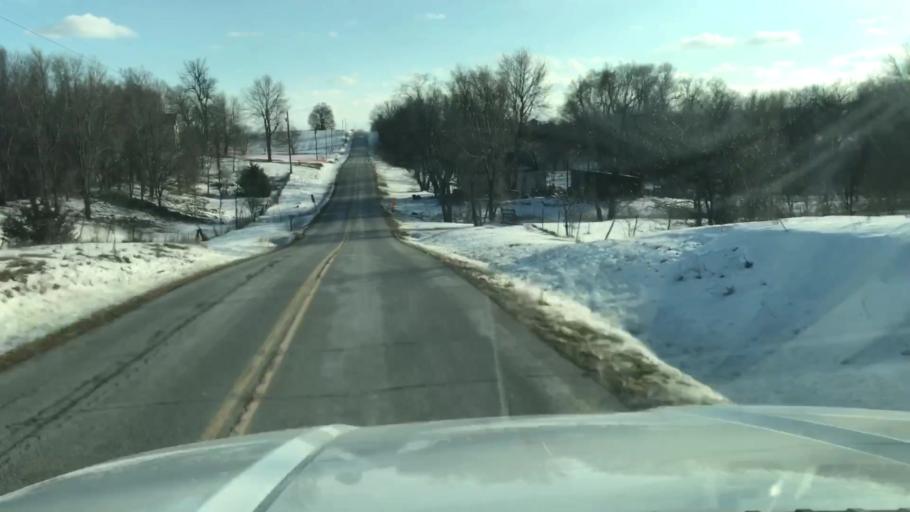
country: US
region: Missouri
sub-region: Holt County
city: Oregon
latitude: 40.0604
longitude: -94.9749
